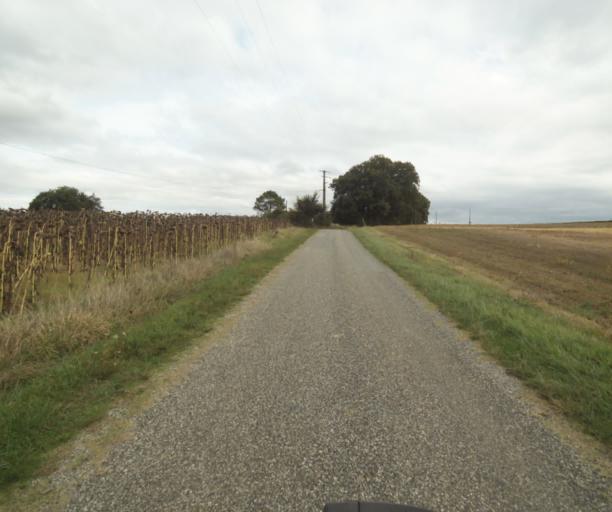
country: FR
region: Midi-Pyrenees
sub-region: Departement du Tarn-et-Garonne
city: Beaumont-de-Lomagne
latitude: 43.8255
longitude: 1.0789
